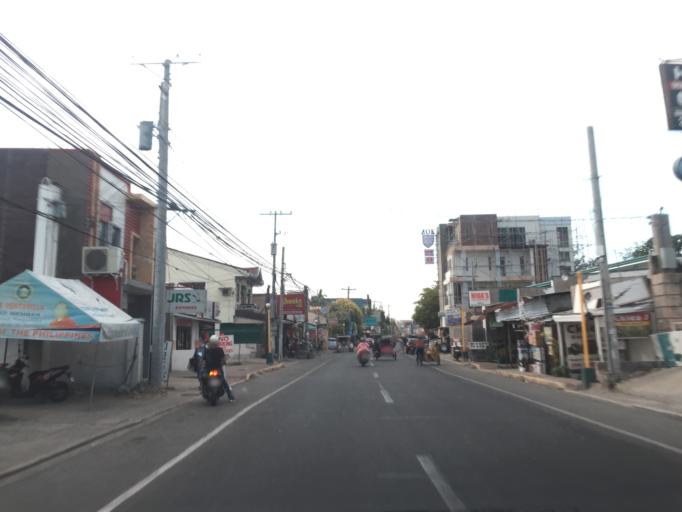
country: PH
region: Ilocos
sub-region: Province of Pangasinan
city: Bolingit
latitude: 15.9291
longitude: 120.3481
